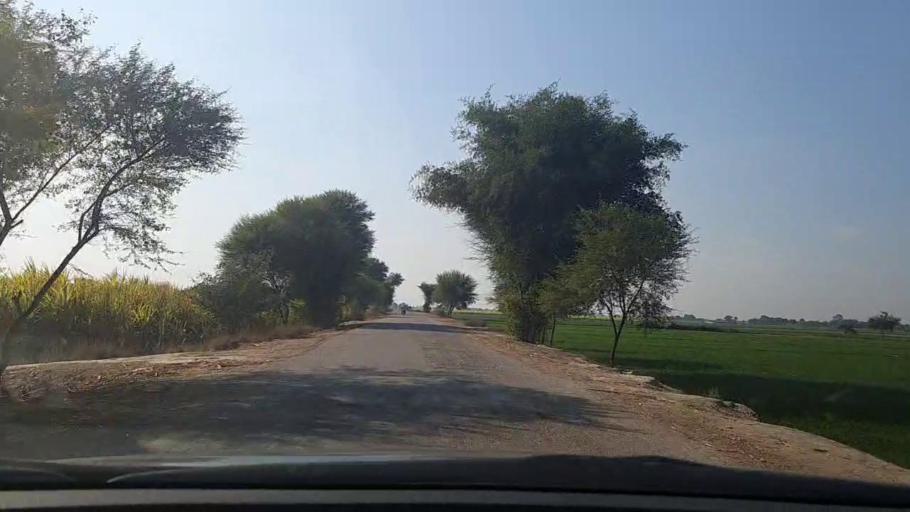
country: PK
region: Sindh
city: Daulatpur
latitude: 26.3199
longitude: 68.0422
